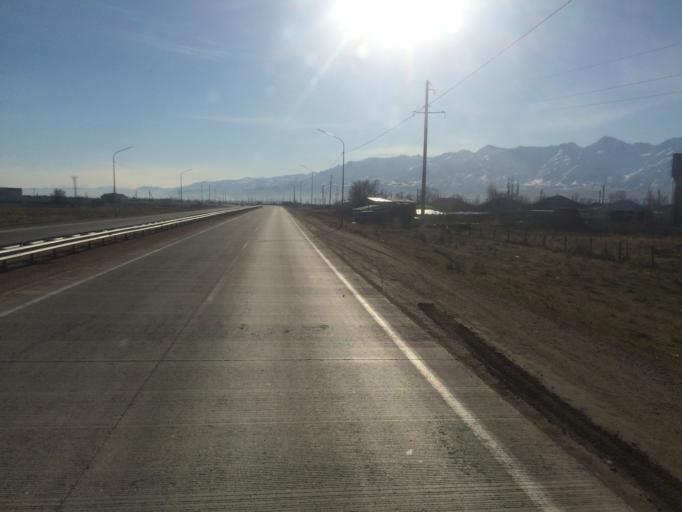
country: KG
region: Talas
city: Ivanovo-Alekseyevka
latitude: 42.9936
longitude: 72.1105
